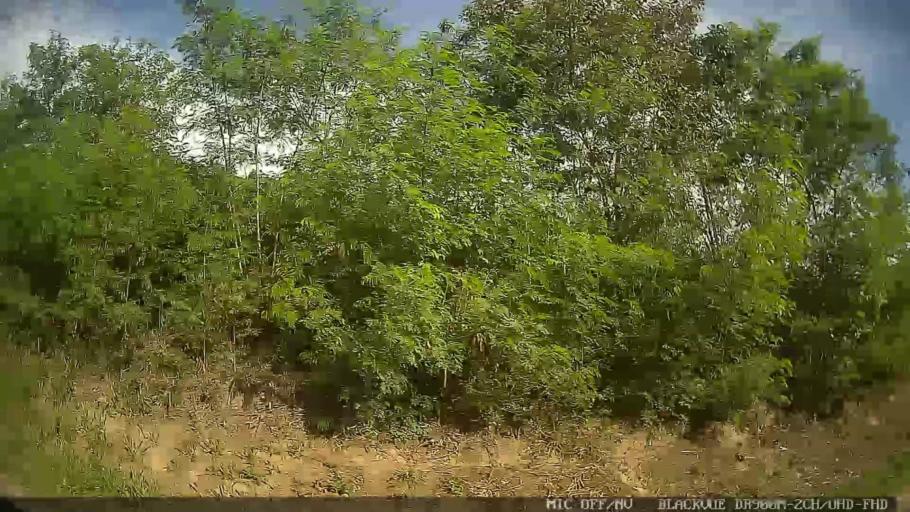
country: BR
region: Sao Paulo
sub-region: Tiete
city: Tiete
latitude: -23.0993
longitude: -47.6906
